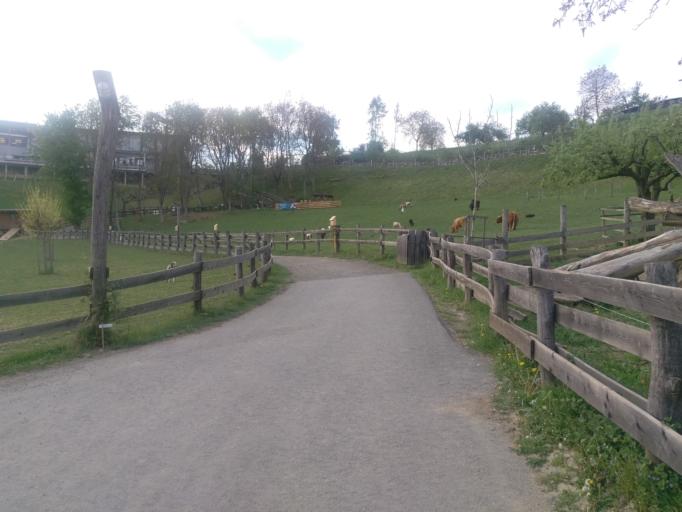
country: AT
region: Styria
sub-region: Politischer Bezirk Suedoststeiermark
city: Riegersburg
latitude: 46.9910
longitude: 15.9107
